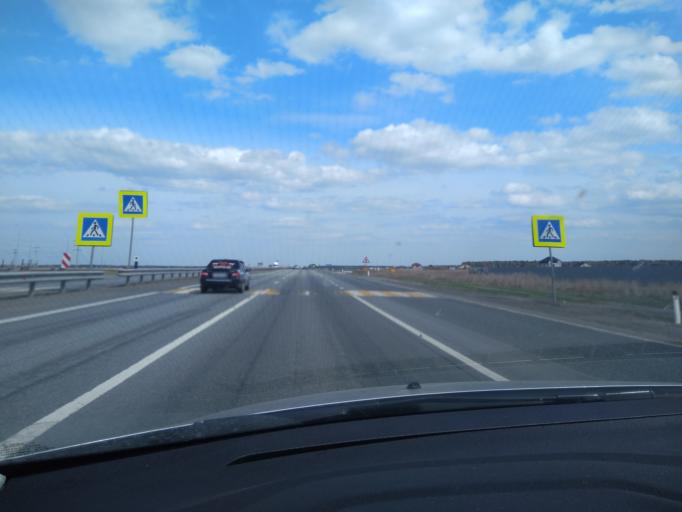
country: RU
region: Tjumen
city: Moskovskiy
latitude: 57.0939
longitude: 65.1595
